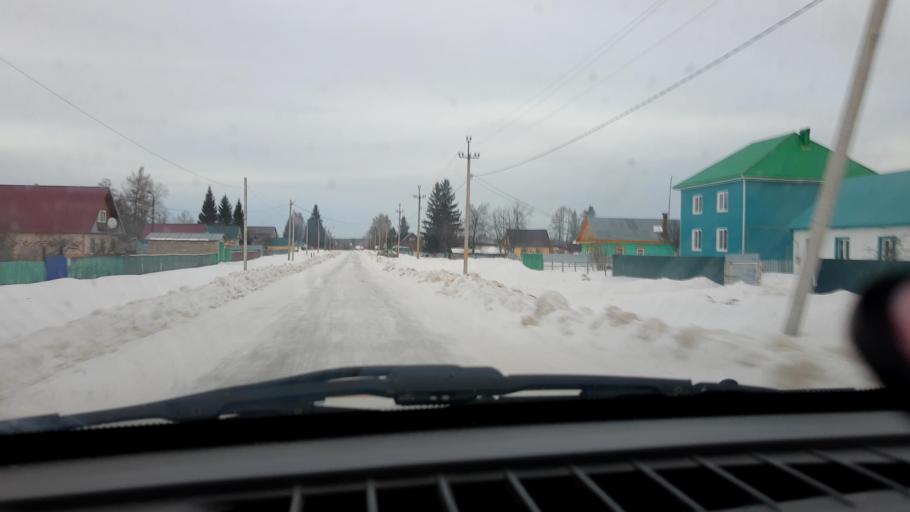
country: RU
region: Bashkortostan
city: Urman
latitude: 54.8681
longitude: 56.8654
